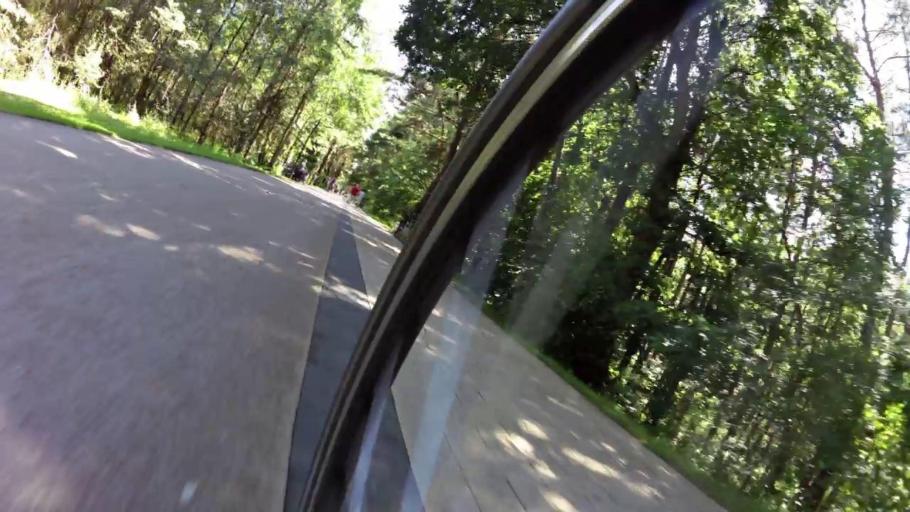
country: PL
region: West Pomeranian Voivodeship
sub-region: Swinoujscie
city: Swinoujscie
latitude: 53.9298
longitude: 14.2173
